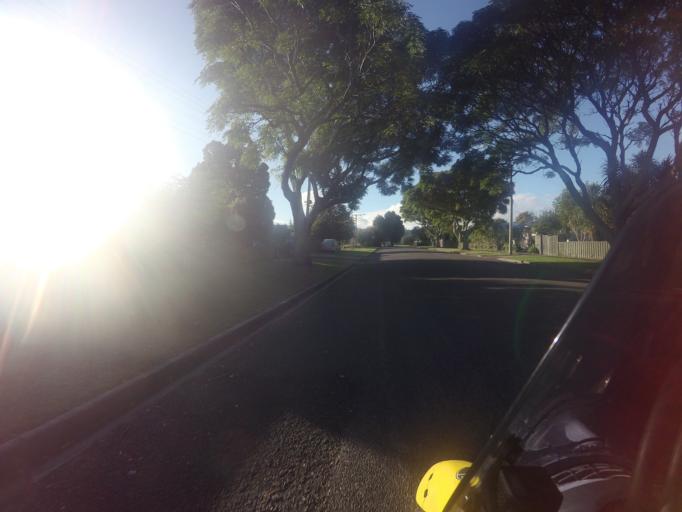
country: NZ
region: Gisborne
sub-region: Gisborne District
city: Gisborne
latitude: -38.6684
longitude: 178.0509
